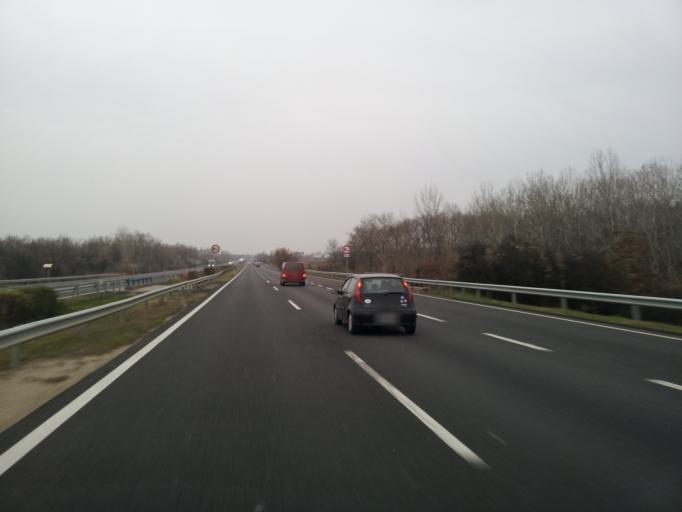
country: HU
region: Fejer
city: Pakozd
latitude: 47.2238
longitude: 18.5688
